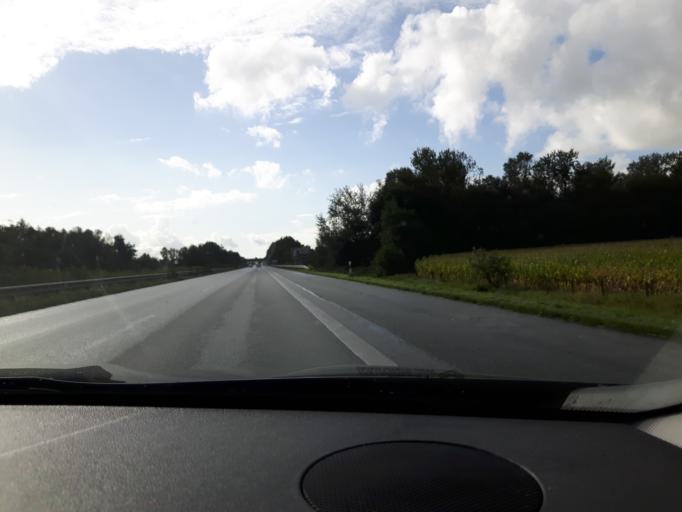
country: DE
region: Schleswig-Holstein
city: Handewitt
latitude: 54.7936
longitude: 9.3343
